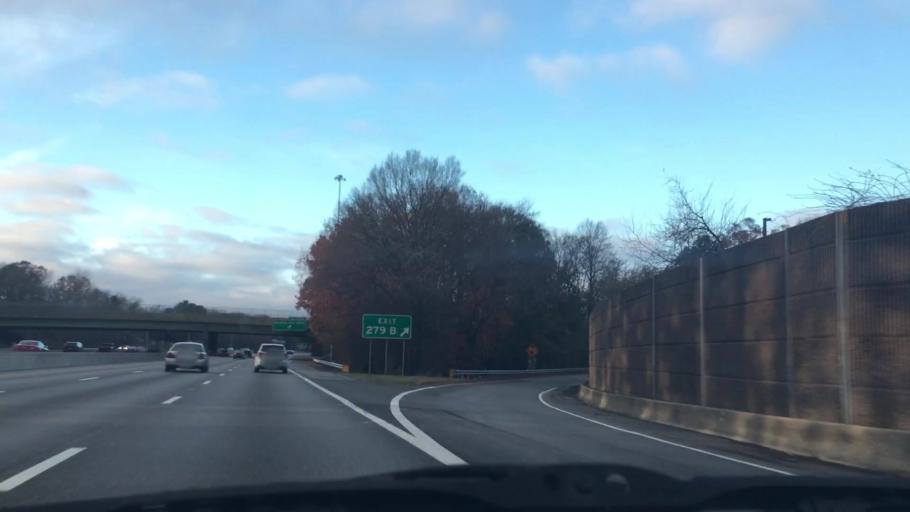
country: US
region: Virginia
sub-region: City of Norfolk
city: Norfolk
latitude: 36.8900
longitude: -76.2300
